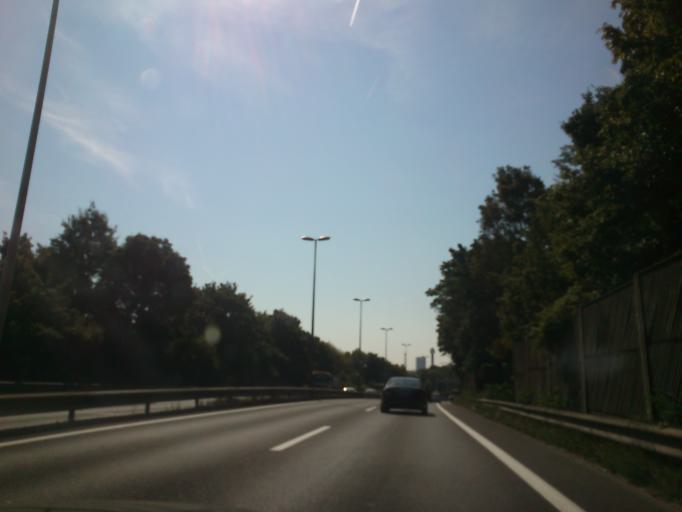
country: AT
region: Upper Austria
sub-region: Linz Stadt
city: Linz
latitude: 48.3131
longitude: 14.3084
